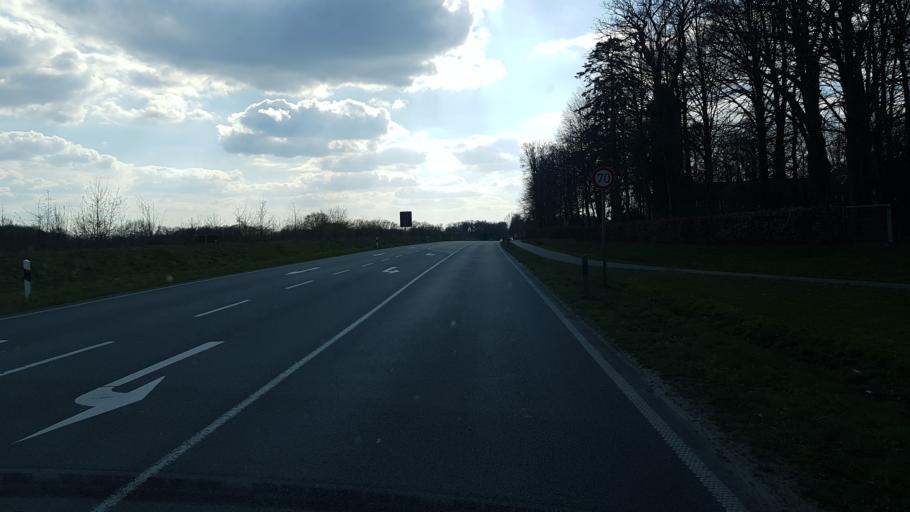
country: DE
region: Lower Saxony
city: Rastede
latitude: 53.2299
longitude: 8.2661
